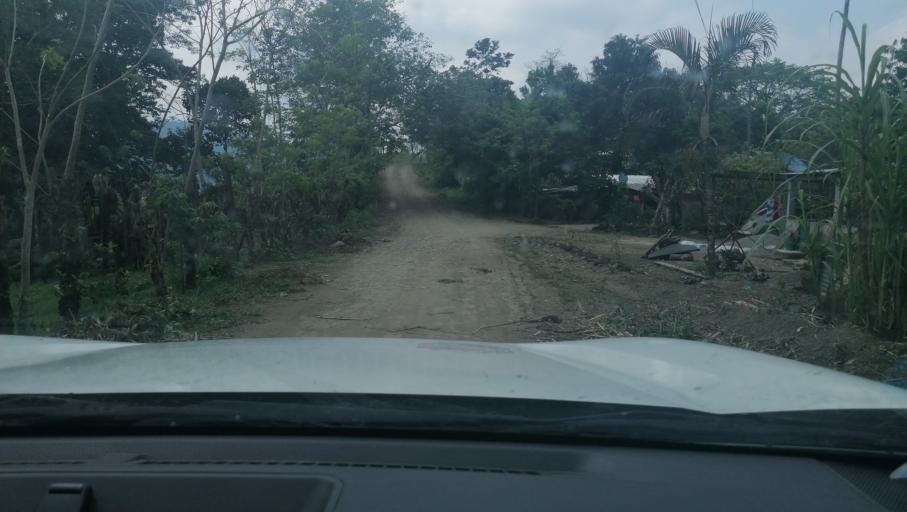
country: MX
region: Chiapas
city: Ostuacan
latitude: 17.3618
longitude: -93.3260
